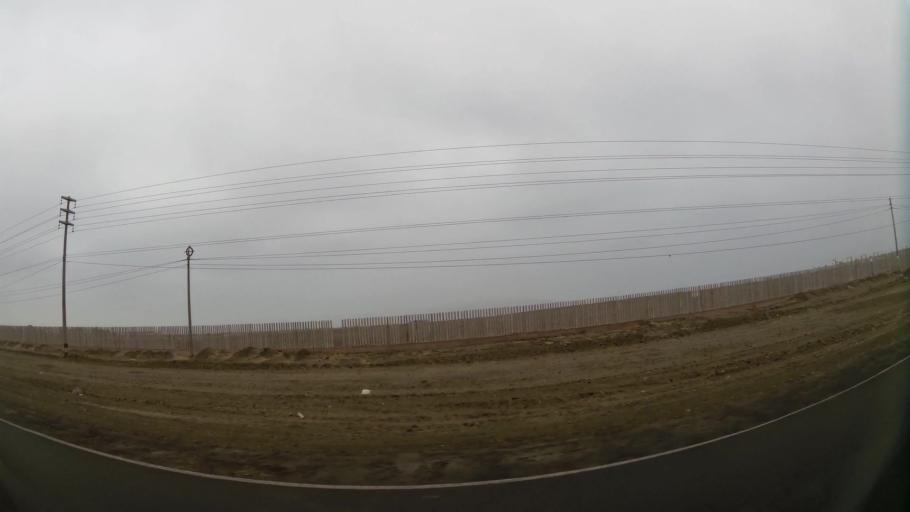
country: PE
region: Ica
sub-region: Provincia de Pisco
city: Paracas
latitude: -13.8139
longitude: -76.2428
